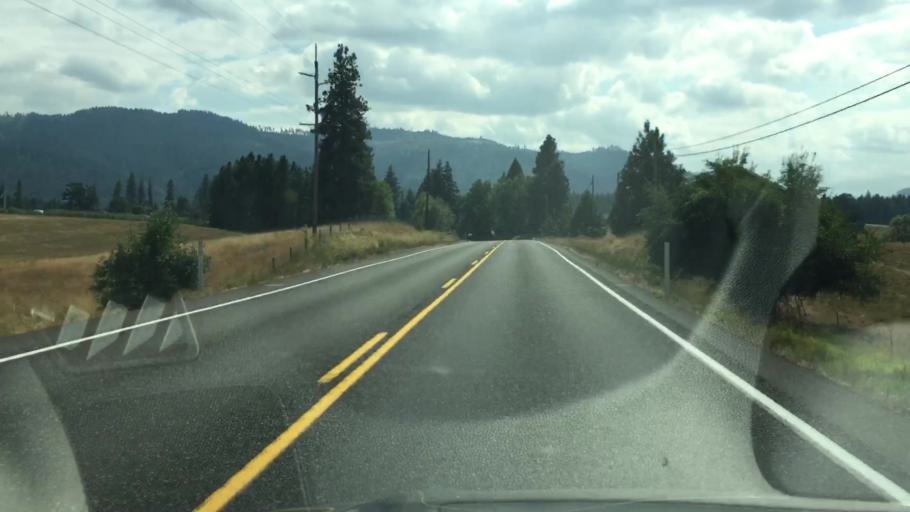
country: US
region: Washington
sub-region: Klickitat County
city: White Salmon
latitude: 45.8111
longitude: -121.4903
